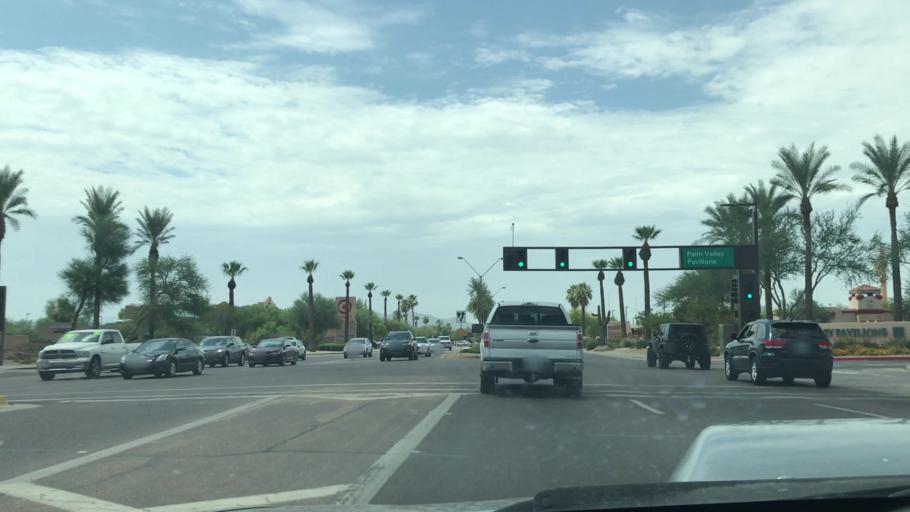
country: US
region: Arizona
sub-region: Maricopa County
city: Goodyear
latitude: 33.4628
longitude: -112.3582
